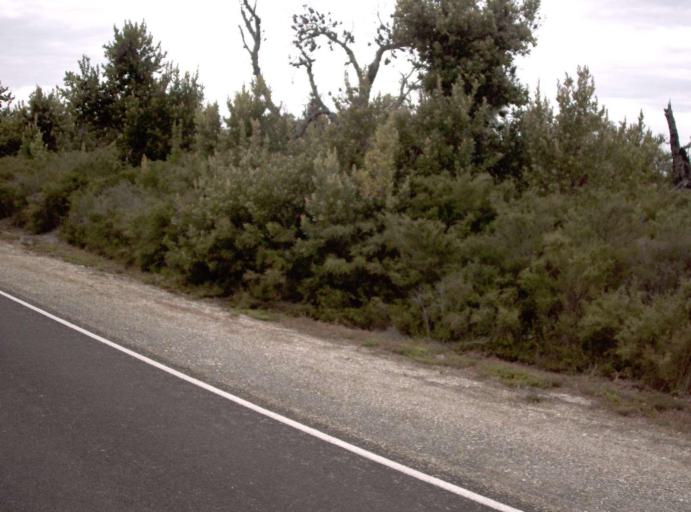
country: AU
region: Victoria
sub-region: Wellington
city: Sale
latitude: -38.1945
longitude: 147.3633
